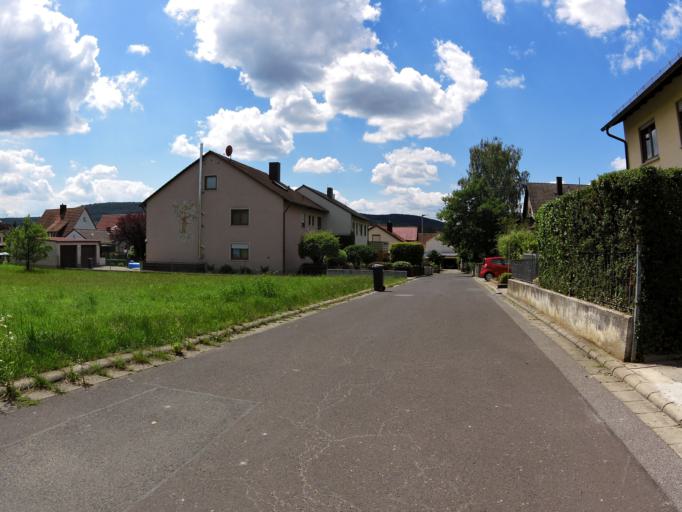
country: DE
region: Bavaria
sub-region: Regierungsbezirk Unterfranken
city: Thungersheim
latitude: 49.8832
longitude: 9.8443
